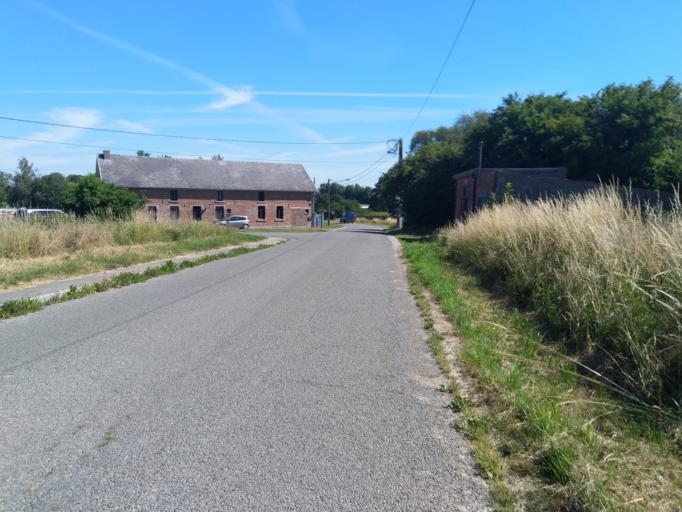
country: BE
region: Wallonia
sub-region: Province du Hainaut
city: Frameries
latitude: 50.3642
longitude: 3.8721
